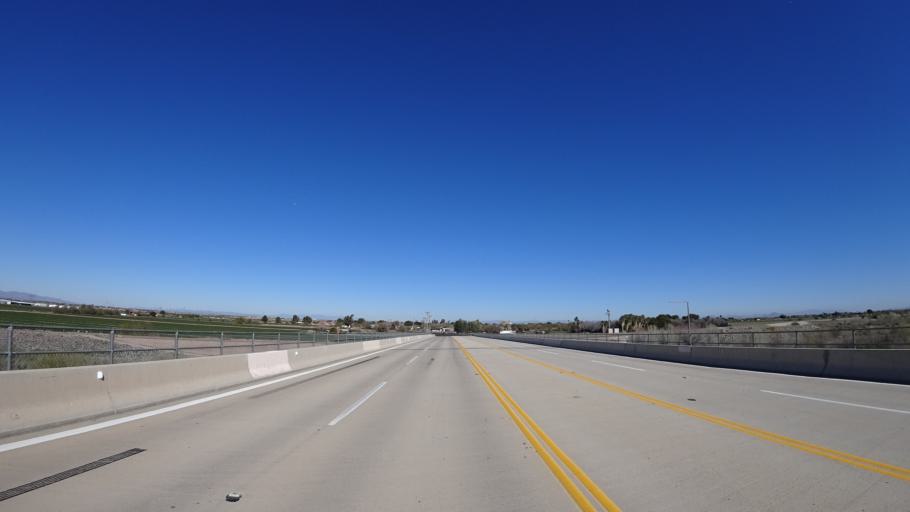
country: US
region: Arizona
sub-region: Maricopa County
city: Avondale
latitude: 33.3848
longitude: -112.3072
